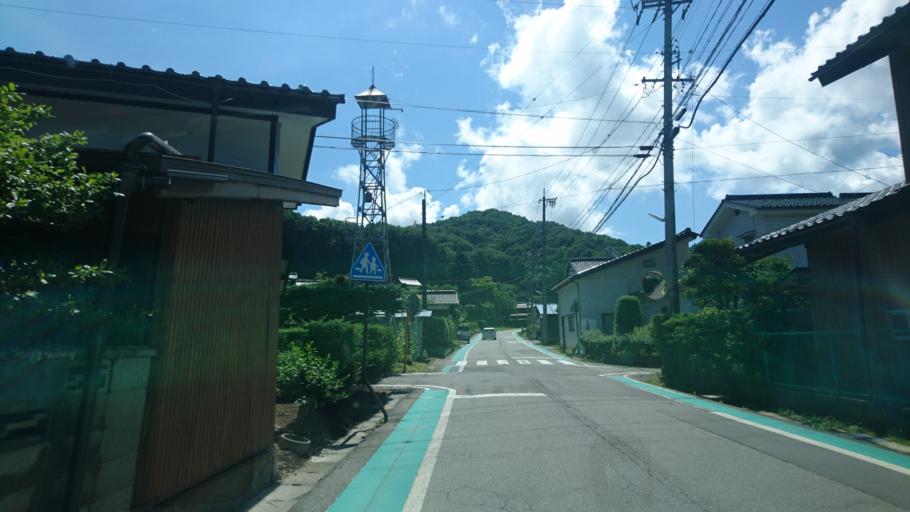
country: JP
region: Nagano
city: Saku
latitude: 36.3026
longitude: 138.6023
